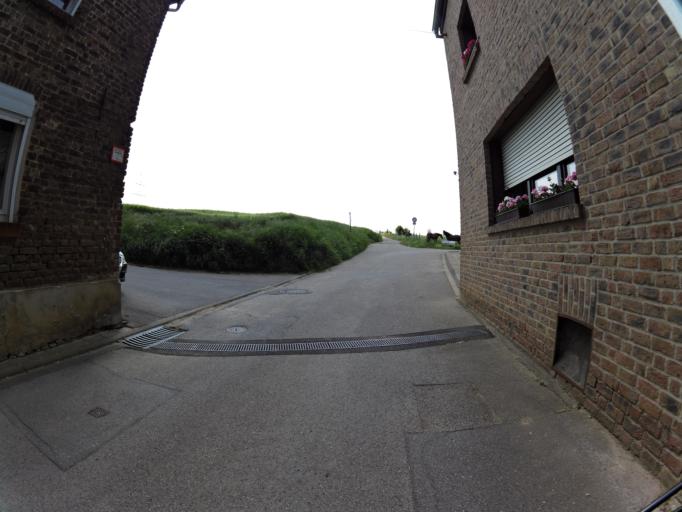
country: DE
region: North Rhine-Westphalia
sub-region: Regierungsbezirk Koln
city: Aldenhoven
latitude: 50.9241
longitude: 6.3188
